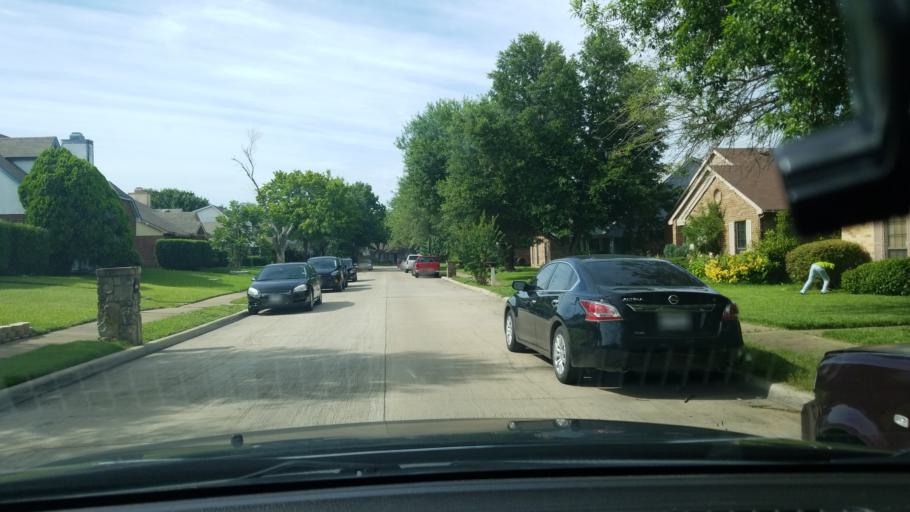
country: US
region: Texas
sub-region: Dallas County
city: Balch Springs
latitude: 32.7725
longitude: -96.6605
